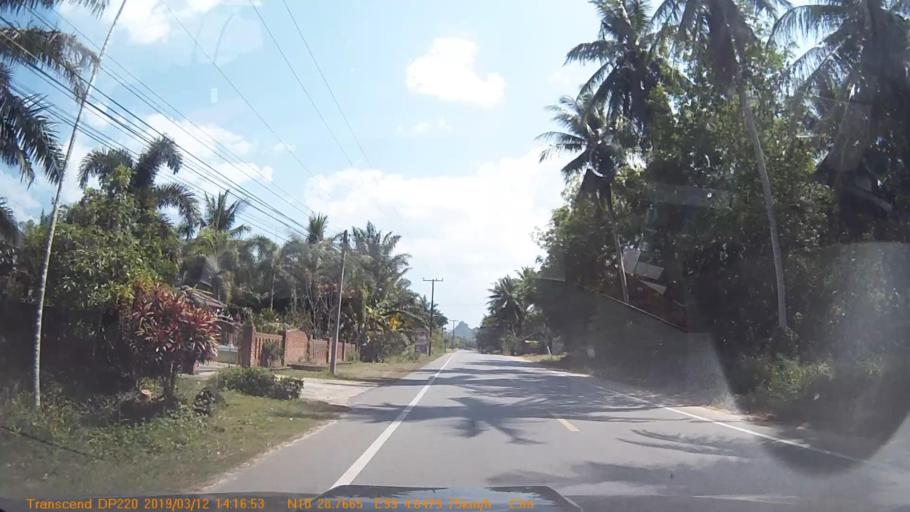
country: TH
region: Chumphon
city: Chumphon
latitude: 10.4791
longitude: 99.0775
